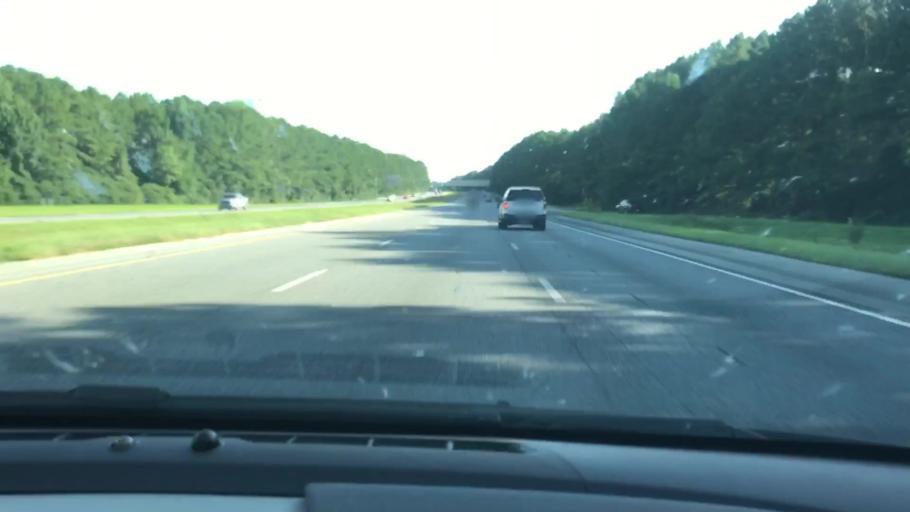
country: US
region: Alabama
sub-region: Russell County
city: Phenix City
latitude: 32.5637
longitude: -84.9625
